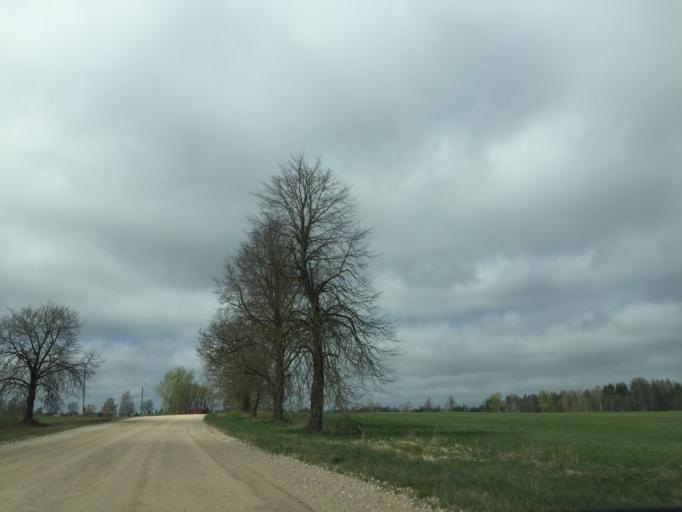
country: EE
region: Valgamaa
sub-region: Valga linn
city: Valga
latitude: 57.5699
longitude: 26.2490
